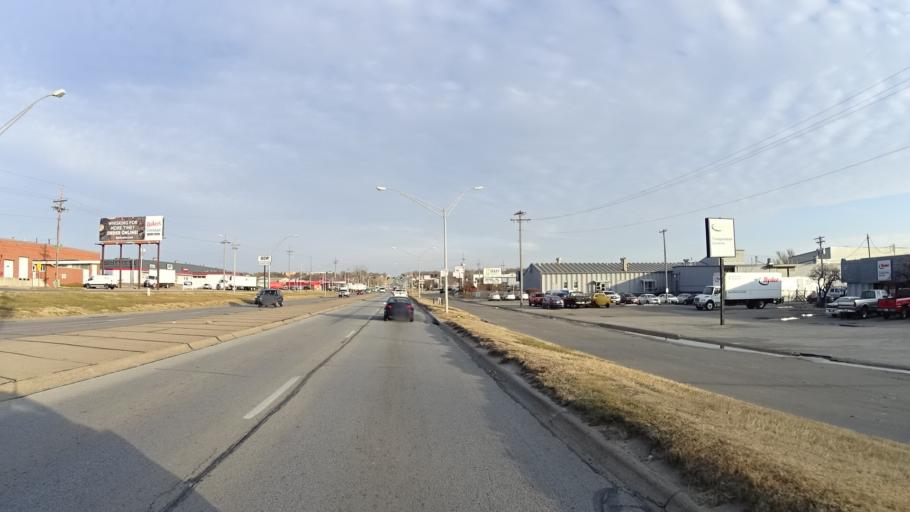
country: US
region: Nebraska
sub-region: Douglas County
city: Ralston
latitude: 41.2124
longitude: -96.0184
